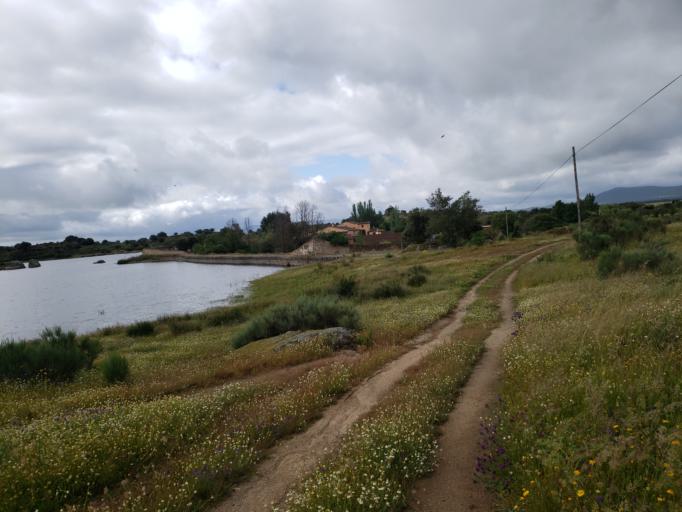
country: ES
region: Extremadura
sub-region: Provincia de Caceres
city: Malpartida de Caceres
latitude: 39.4247
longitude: -6.5041
